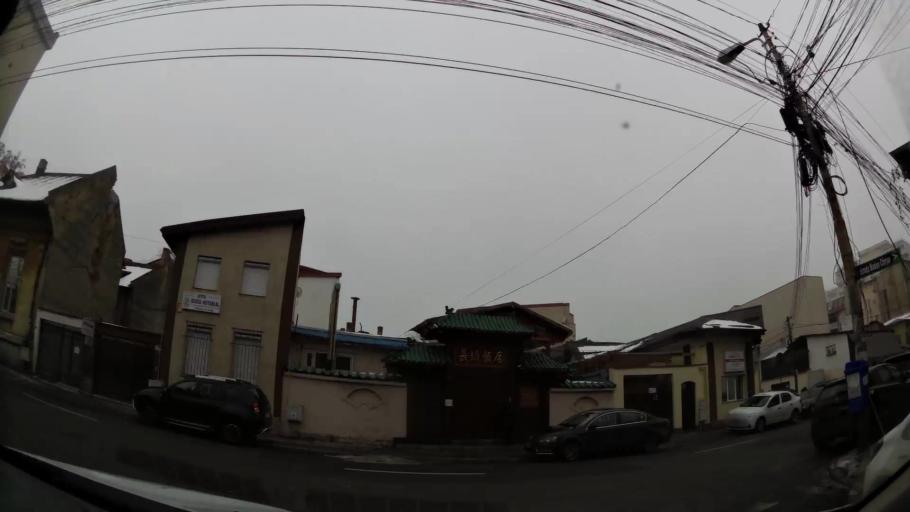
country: RO
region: Bucuresti
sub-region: Municipiul Bucuresti
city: Bucharest
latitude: 44.4506
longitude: 26.1118
